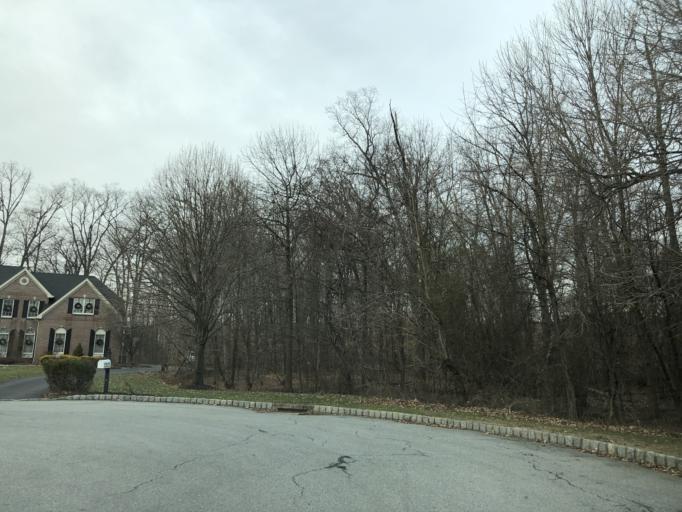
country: US
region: Pennsylvania
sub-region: Chester County
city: Exton
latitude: 40.0369
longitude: -75.6213
